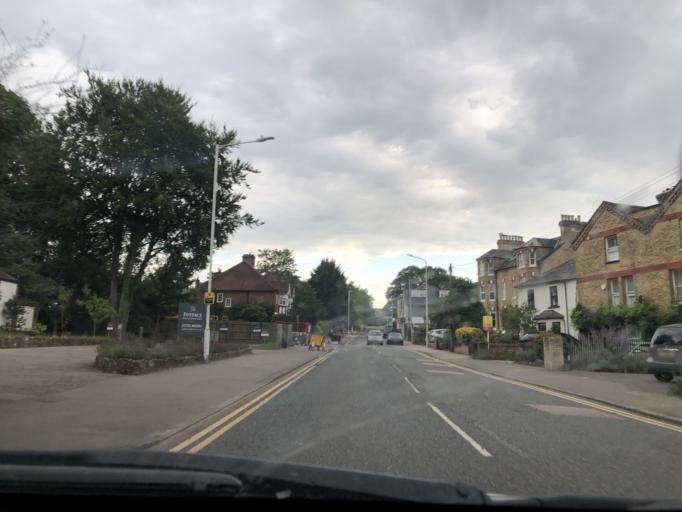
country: GB
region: England
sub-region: Kent
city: Sevenoaks
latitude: 51.2787
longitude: 0.1941
